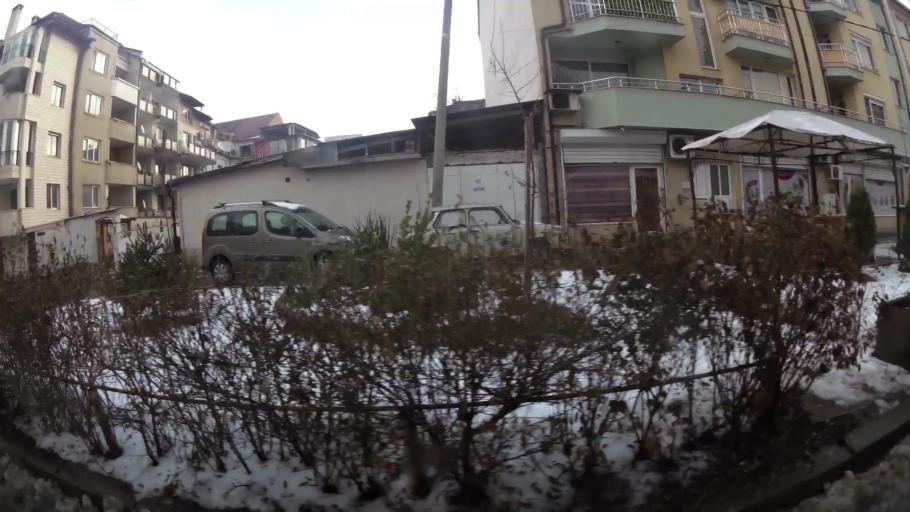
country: BG
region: Sofia-Capital
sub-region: Stolichna Obshtina
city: Sofia
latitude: 42.6986
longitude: 23.2812
